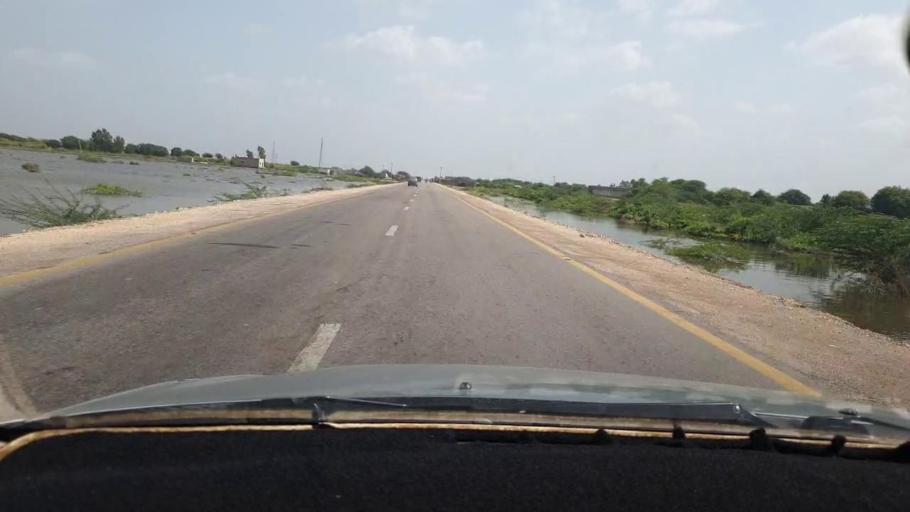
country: PK
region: Sindh
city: Digri
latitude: 25.1217
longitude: 69.1492
